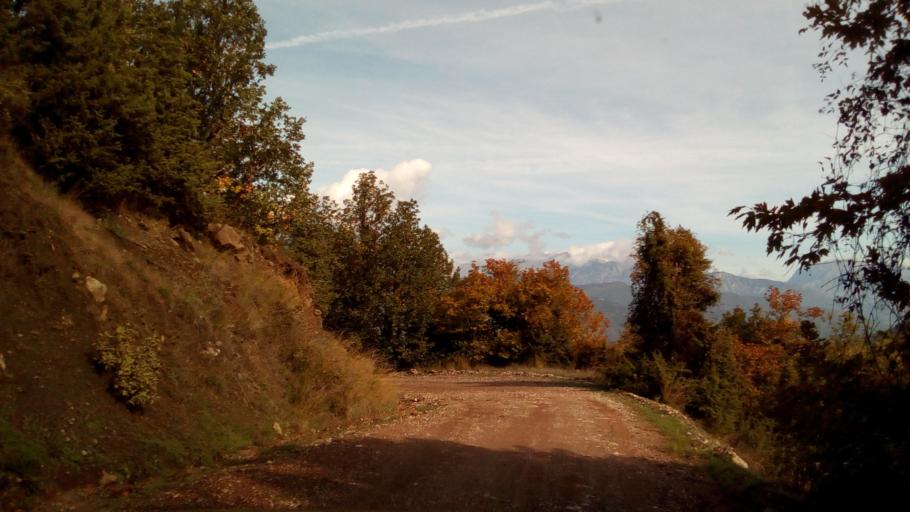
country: GR
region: West Greece
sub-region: Nomos Achaias
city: Kamarai
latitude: 38.4780
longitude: 22.0251
